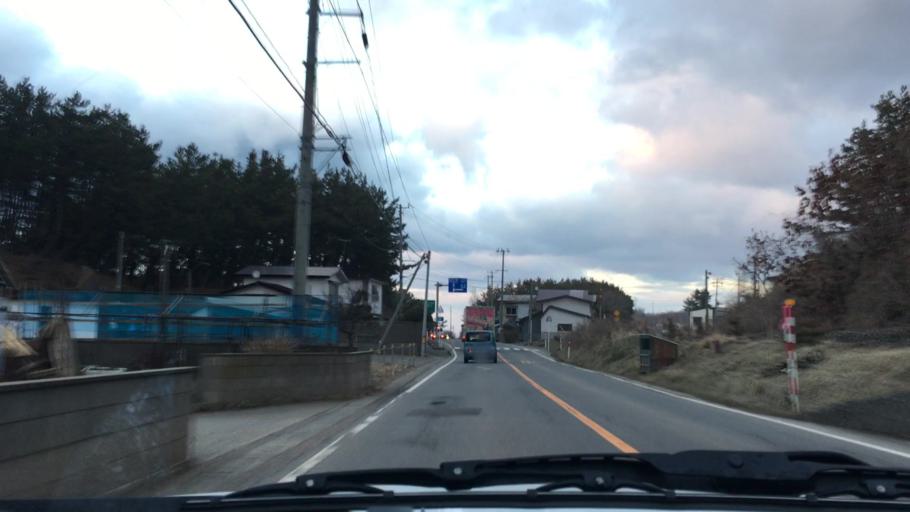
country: JP
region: Aomori
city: Shimokizukuri
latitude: 40.7570
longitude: 140.1539
